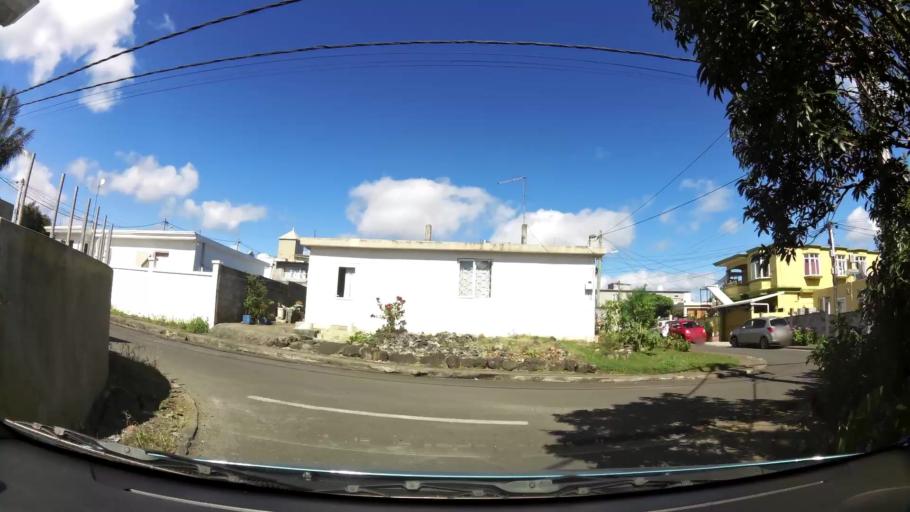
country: MU
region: Plaines Wilhems
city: Vacoas
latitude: -20.3050
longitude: 57.4724
